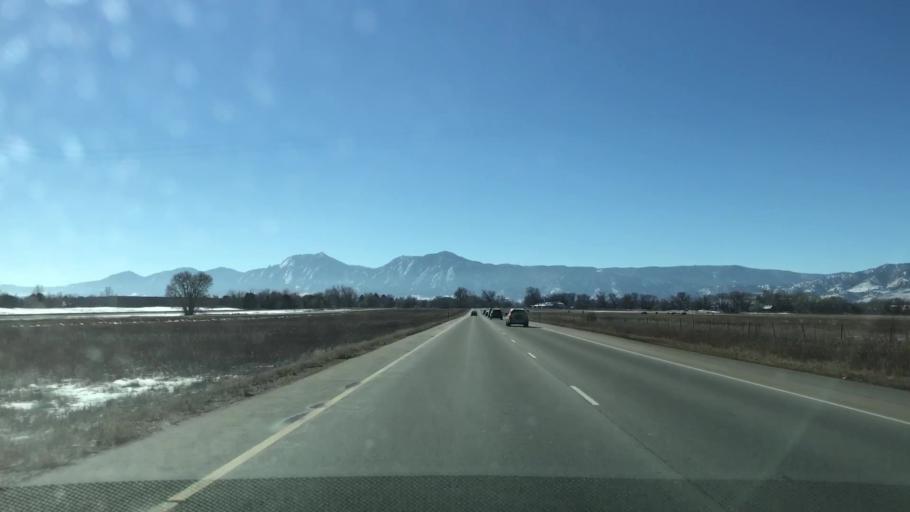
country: US
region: Colorado
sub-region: Boulder County
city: Gunbarrel
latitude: 40.0654
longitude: -105.2174
